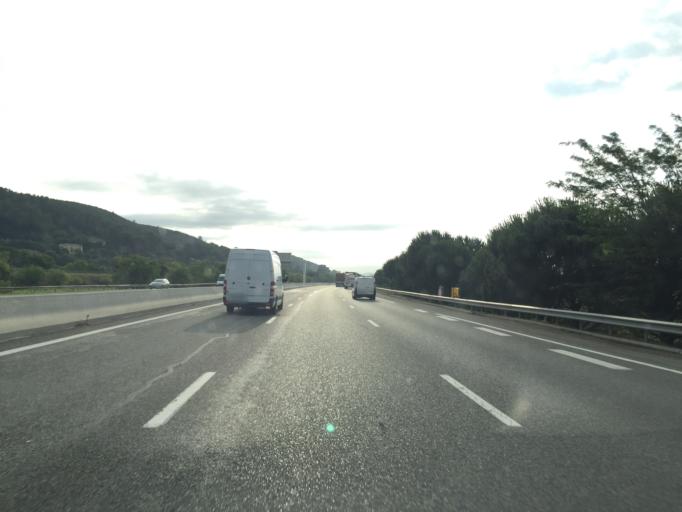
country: FR
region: Provence-Alpes-Cote d'Azur
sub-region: Departement du Var
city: Le Cannet-des-Maures
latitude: 43.4007
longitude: 6.3641
